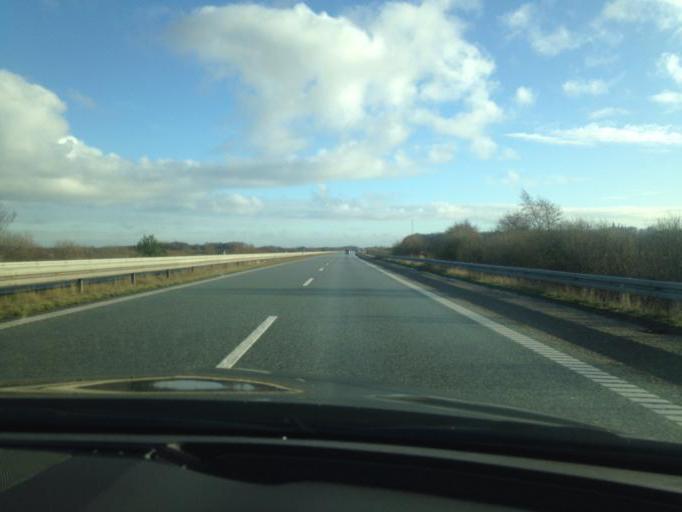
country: DK
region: South Denmark
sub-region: Vejen Kommune
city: Brorup
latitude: 55.5017
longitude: 9.0586
